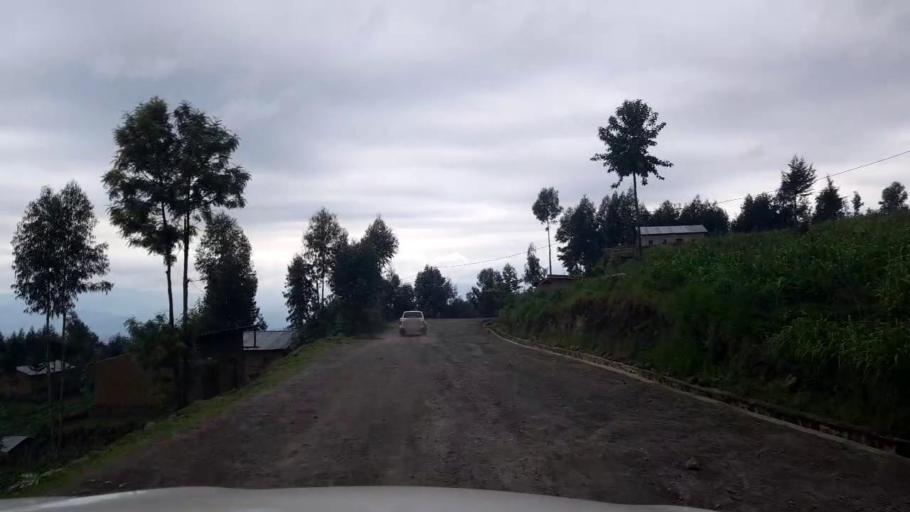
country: RW
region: Northern Province
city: Musanze
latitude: -1.4897
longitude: 29.5305
